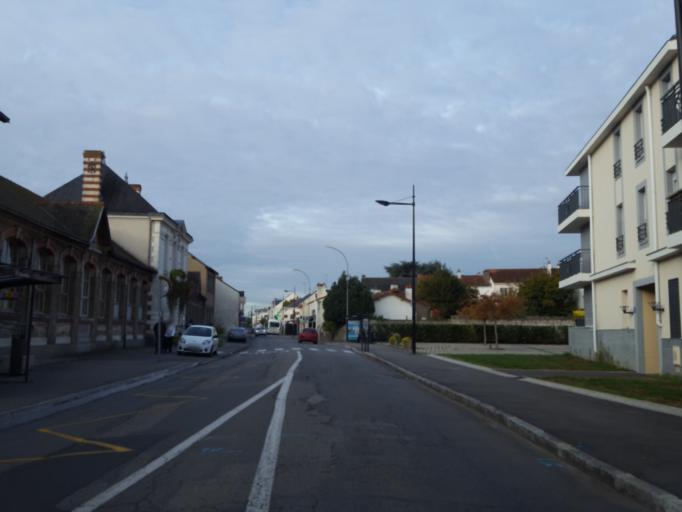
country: FR
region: Pays de la Loire
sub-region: Departement de la Loire-Atlantique
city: Saint-Sebastien-sur-Loire
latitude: 47.2076
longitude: -1.5027
